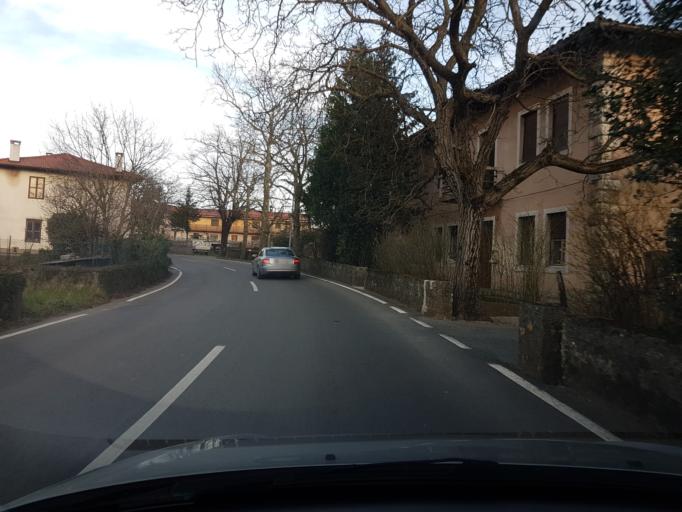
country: SI
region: Divaca
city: Divaca
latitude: 45.6608
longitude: 13.9254
